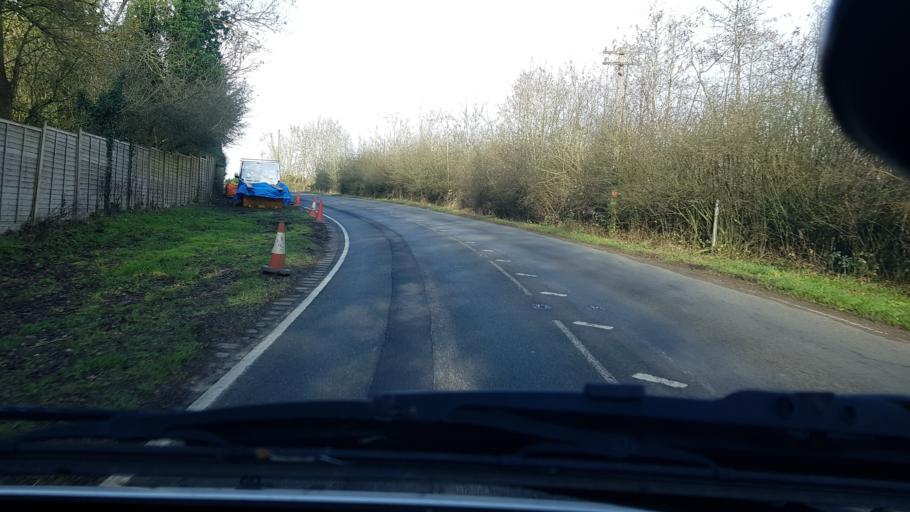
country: GB
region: England
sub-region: Surrey
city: Normandy
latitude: 51.2394
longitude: -0.6718
